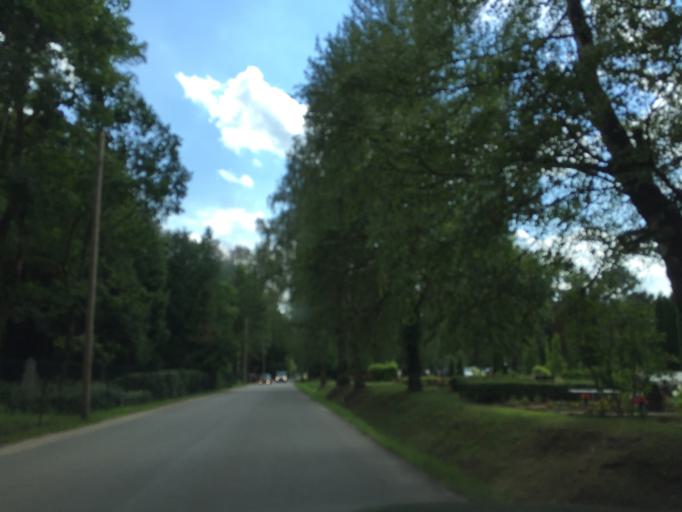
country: LV
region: Jelgava
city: Jelgava
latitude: 56.6269
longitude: 23.6852
